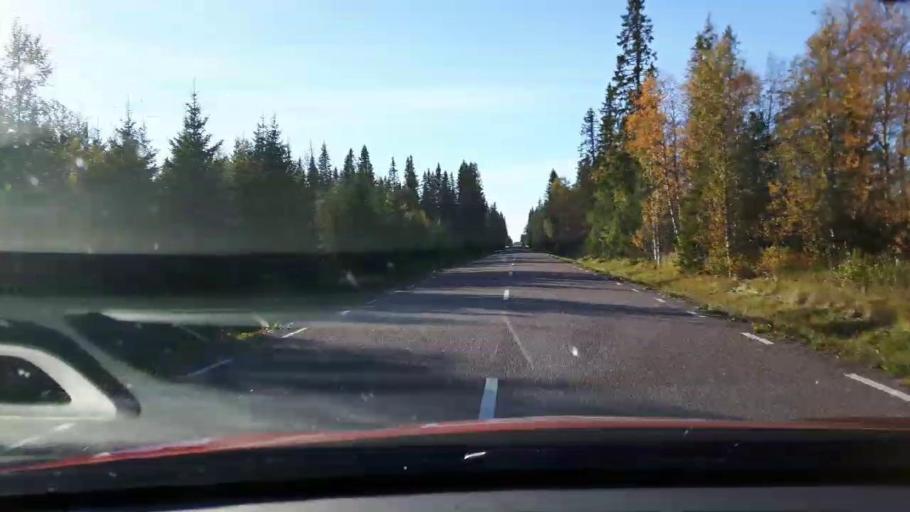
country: SE
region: Jaemtland
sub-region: Stroemsunds Kommun
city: Stroemsund
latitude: 63.8550
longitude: 15.2238
